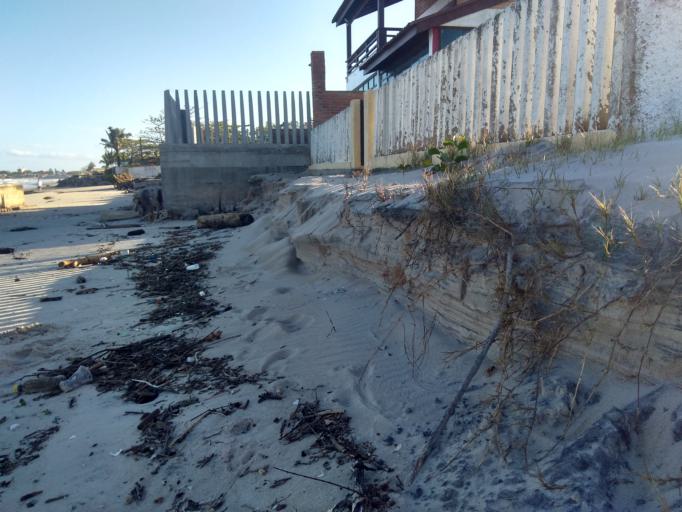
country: BR
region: Parana
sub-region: Guaratuba
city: Guaratuba
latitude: -26.0553
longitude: -48.6112
